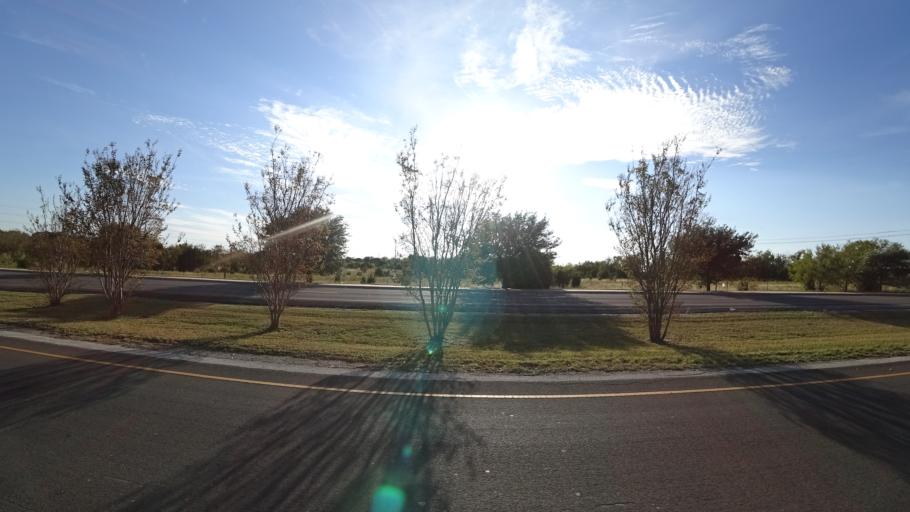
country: US
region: Texas
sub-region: Travis County
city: Pflugerville
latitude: 30.4103
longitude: -97.6495
